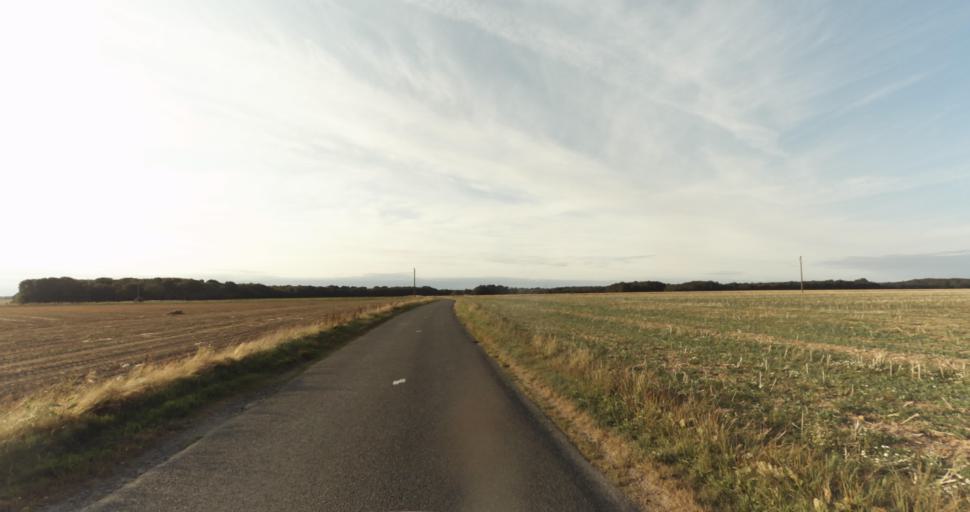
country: FR
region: Haute-Normandie
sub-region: Departement de l'Eure
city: Marcilly-sur-Eure
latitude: 48.8248
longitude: 1.2886
